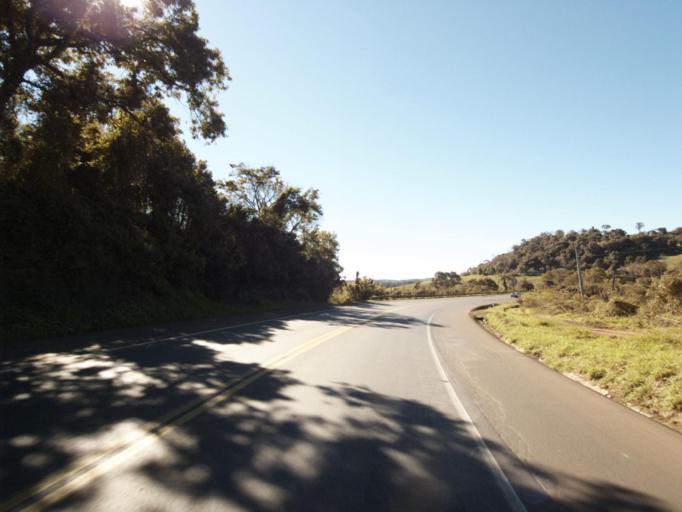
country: BR
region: Santa Catarina
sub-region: Chapeco
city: Chapeco
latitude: -26.9756
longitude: -52.5885
